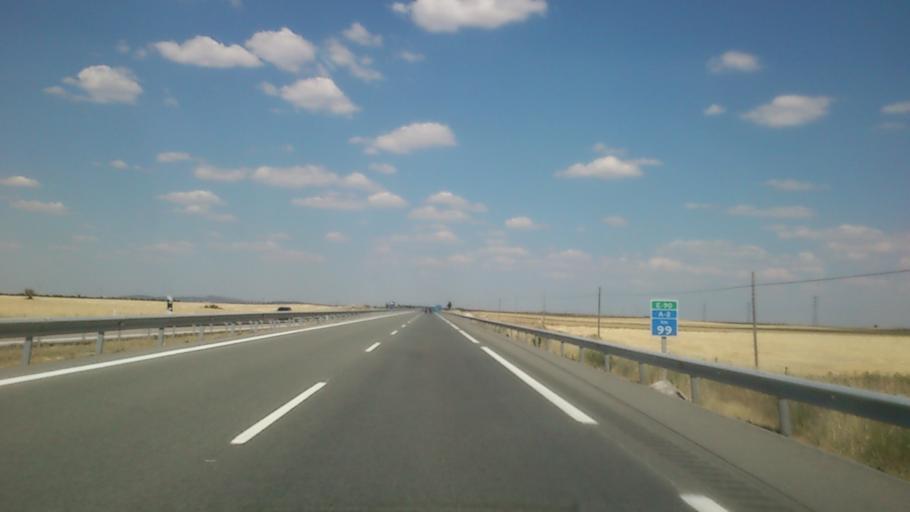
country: ES
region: Castille-La Mancha
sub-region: Provincia de Guadalajara
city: Almadrones
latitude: 40.8820
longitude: -2.7877
